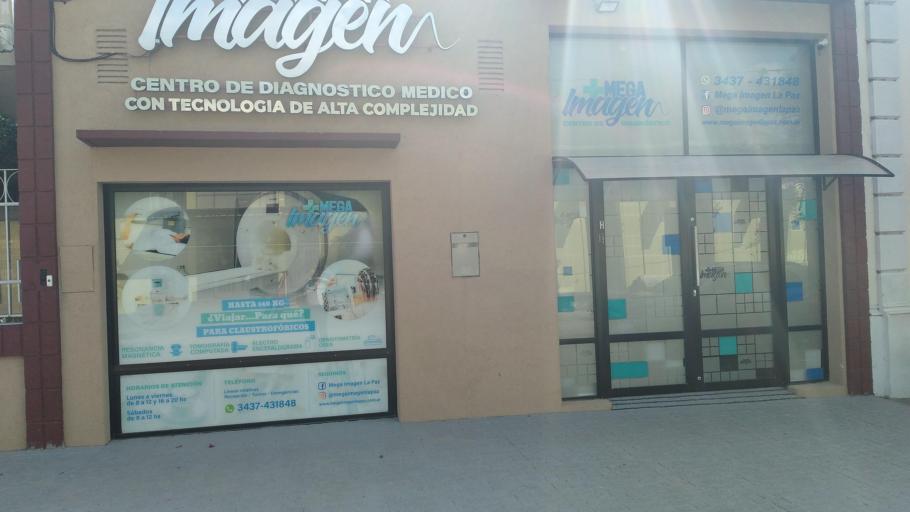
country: AR
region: Entre Rios
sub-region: Departamento de La Paz
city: La Paz
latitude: -30.7377
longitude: -59.6444
